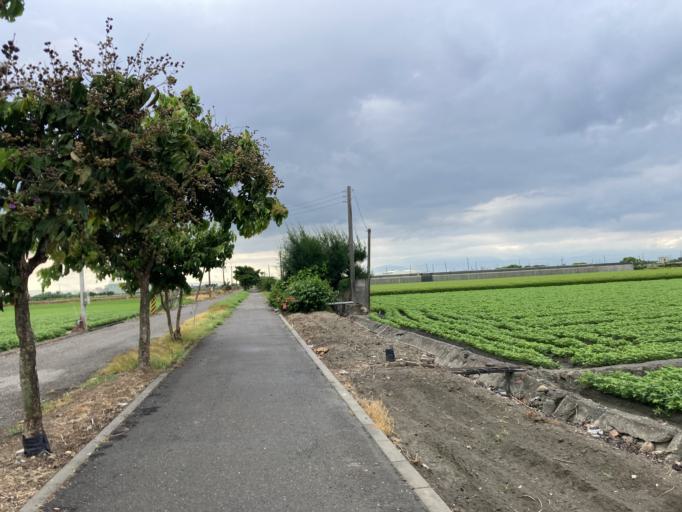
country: TW
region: Taiwan
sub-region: Yunlin
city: Douliu
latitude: 23.8784
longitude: 120.3646
